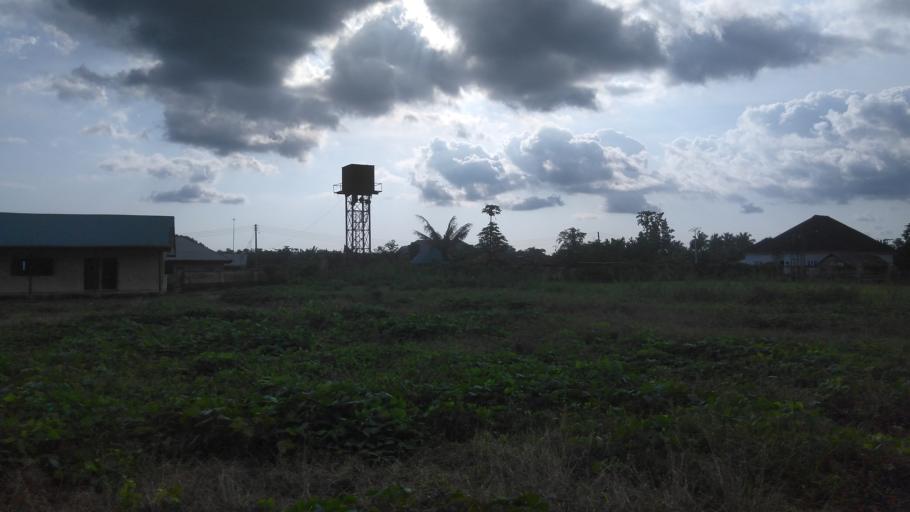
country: NG
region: Edo
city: Siluko
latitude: 6.1436
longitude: 5.2014
